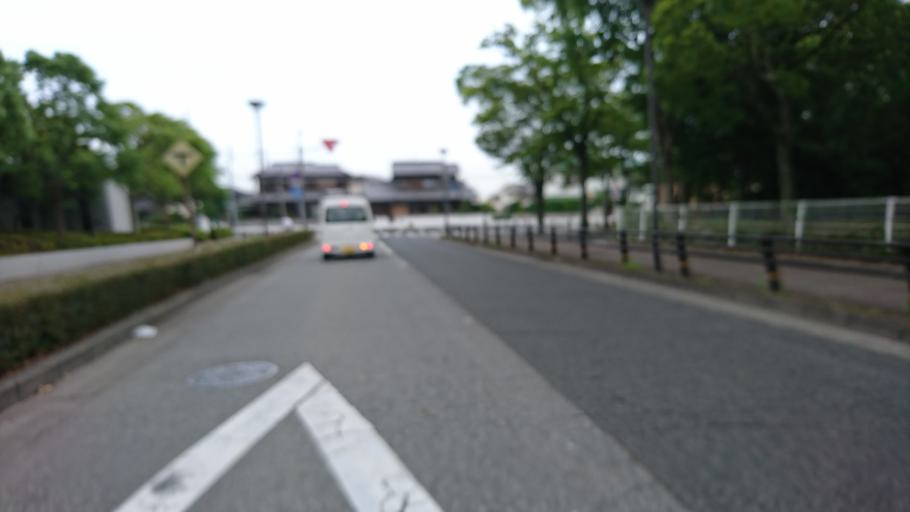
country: JP
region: Hyogo
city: Kakogawacho-honmachi
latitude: 34.7488
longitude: 134.8741
